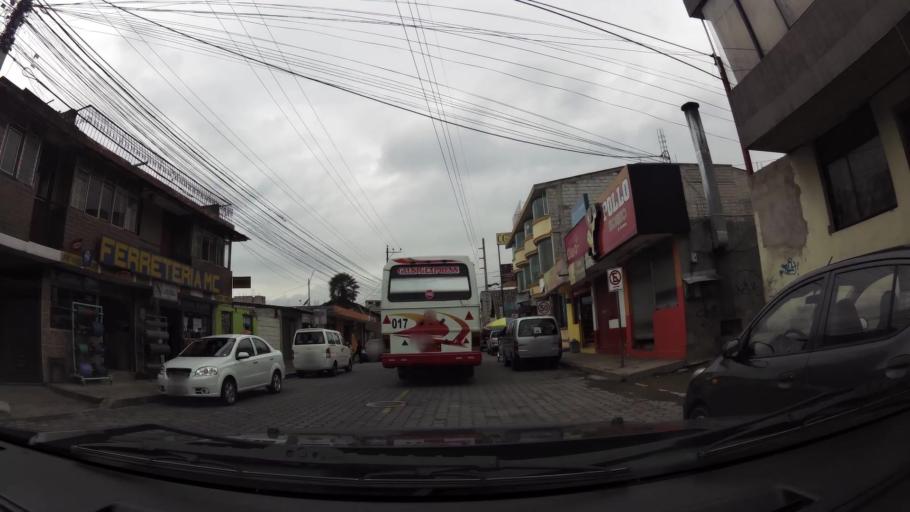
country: EC
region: Pichincha
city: Sangolqui
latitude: -0.3217
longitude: -78.4606
